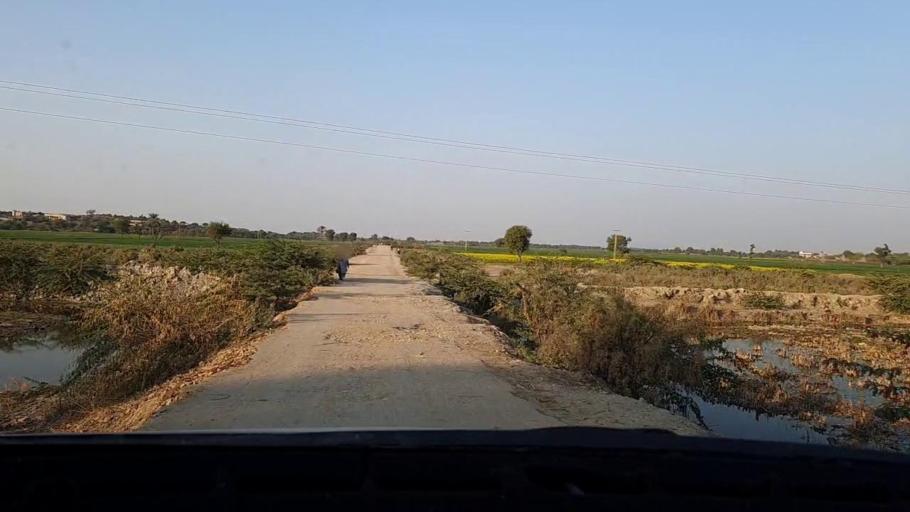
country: PK
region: Sindh
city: Tando Mittha Khan
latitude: 25.8563
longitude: 69.2725
